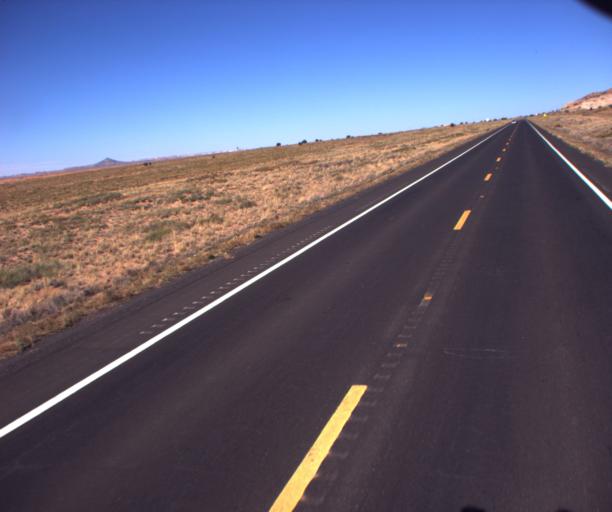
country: US
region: Arizona
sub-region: Coconino County
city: Tuba City
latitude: 36.2295
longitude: -111.0329
